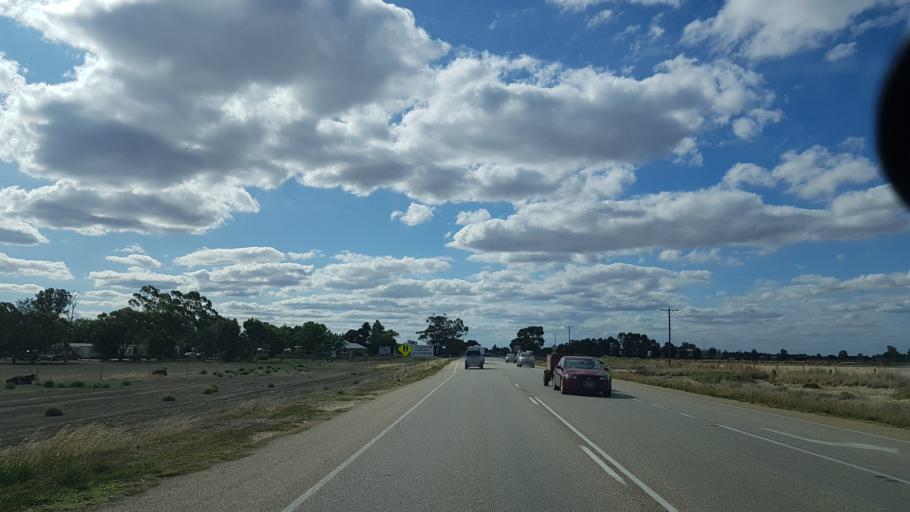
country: AU
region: Victoria
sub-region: Swan Hill
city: Swan Hill
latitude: -35.7622
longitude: 143.9307
